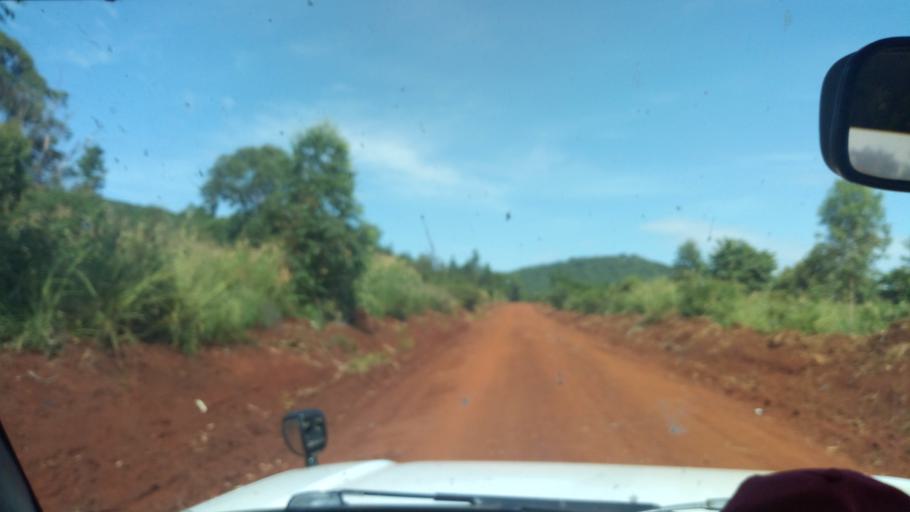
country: UG
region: Western Region
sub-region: Masindi District
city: Masindi
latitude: 1.6523
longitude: 31.7850
